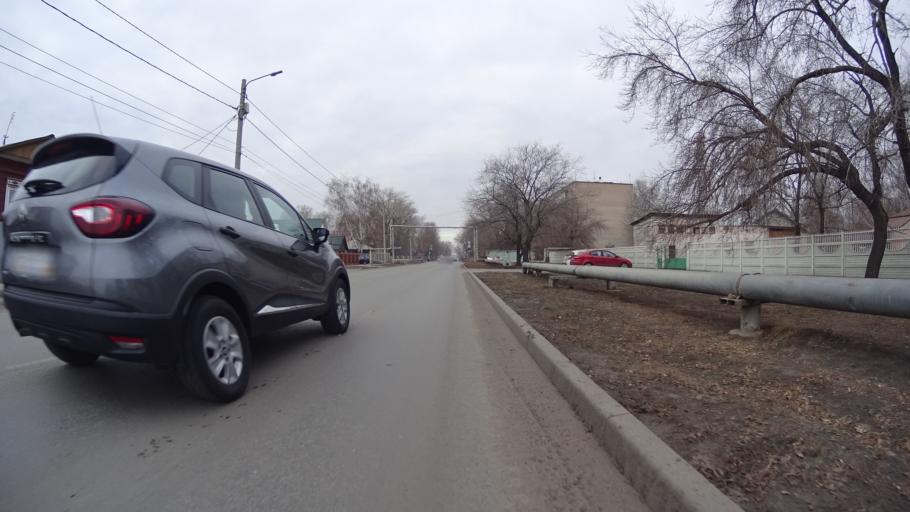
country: RU
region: Chelyabinsk
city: Troitsk
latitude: 54.1104
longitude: 61.5696
